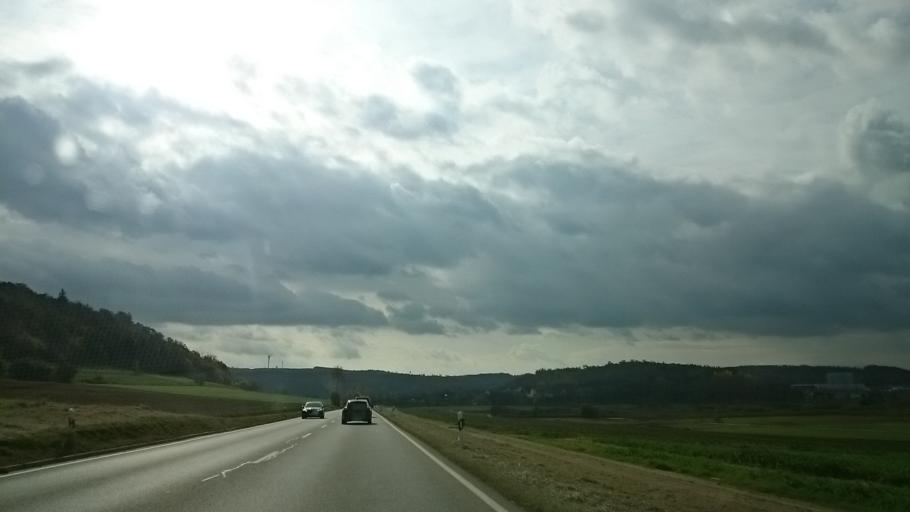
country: DE
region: Bavaria
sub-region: Regierungsbezirk Mittelfranken
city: Treuchtlingen
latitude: 48.9530
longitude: 10.9376
